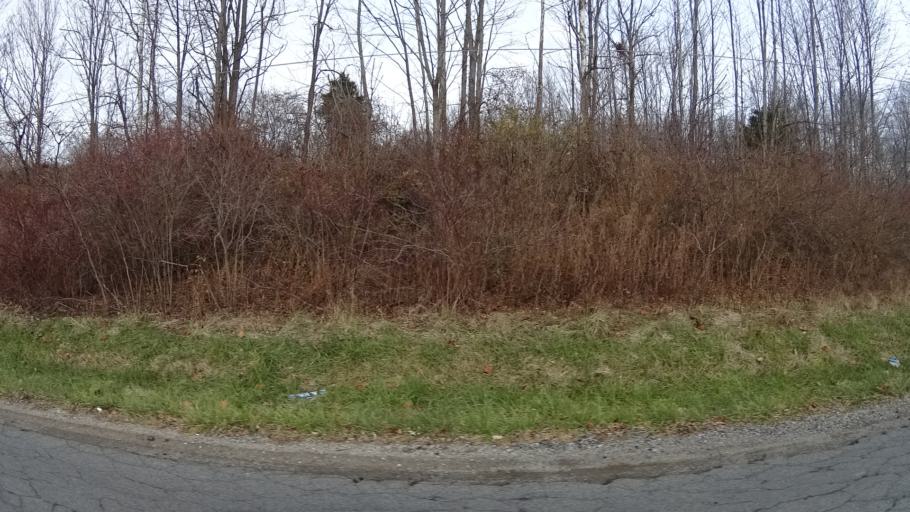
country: US
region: Ohio
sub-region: Lorain County
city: Eaton Estates
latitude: 41.2748
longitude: -81.9279
